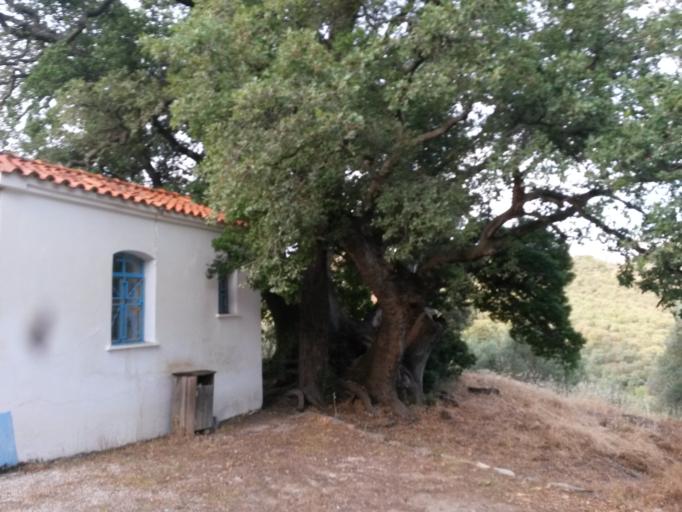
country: GR
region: North Aegean
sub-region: Nomos Lesvou
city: Agiasos
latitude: 39.0988
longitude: 26.3958
